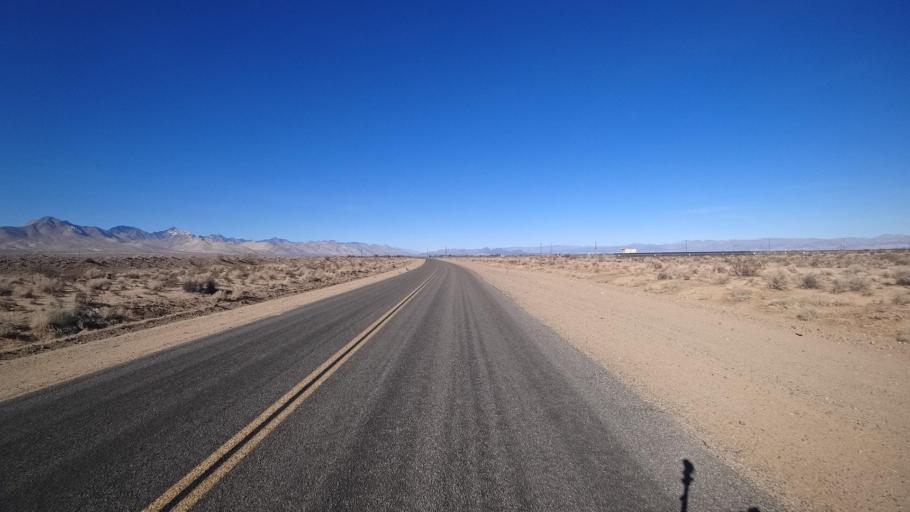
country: US
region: California
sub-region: Kern County
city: Inyokern
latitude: 35.6047
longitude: -117.7990
